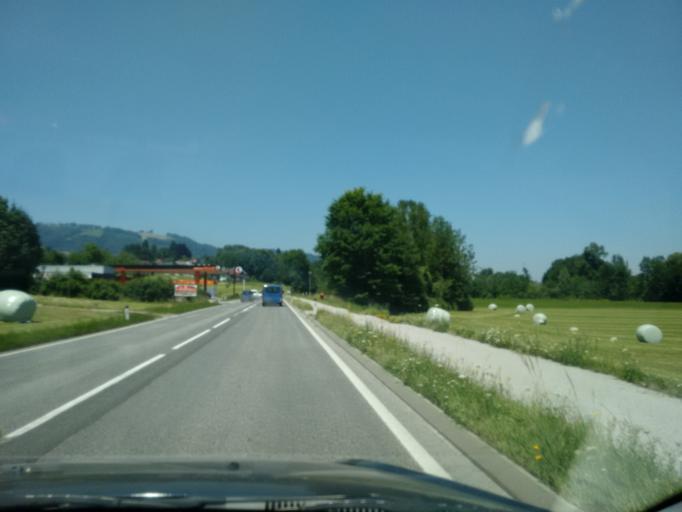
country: AT
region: Upper Austria
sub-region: Politischer Bezirk Gmunden
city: Altmunster
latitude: 47.8840
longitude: 13.7720
